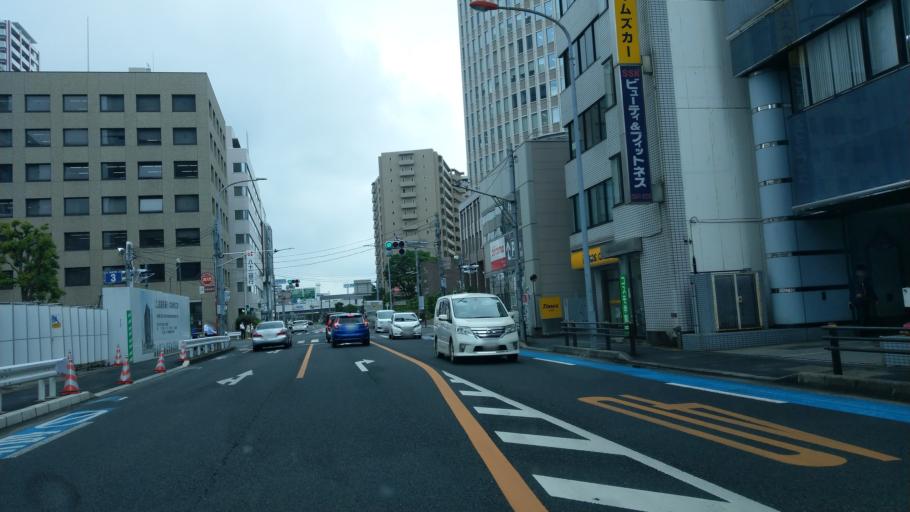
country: JP
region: Saitama
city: Yono
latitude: 35.9048
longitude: 139.6181
